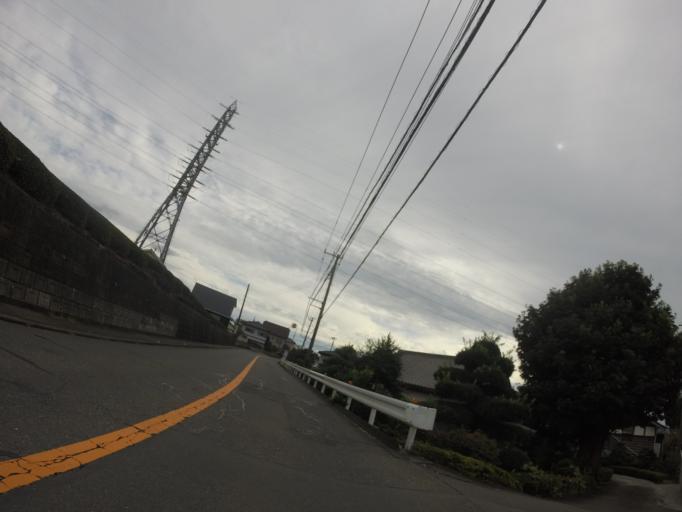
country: JP
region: Shizuoka
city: Fuji
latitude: 35.1881
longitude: 138.7037
